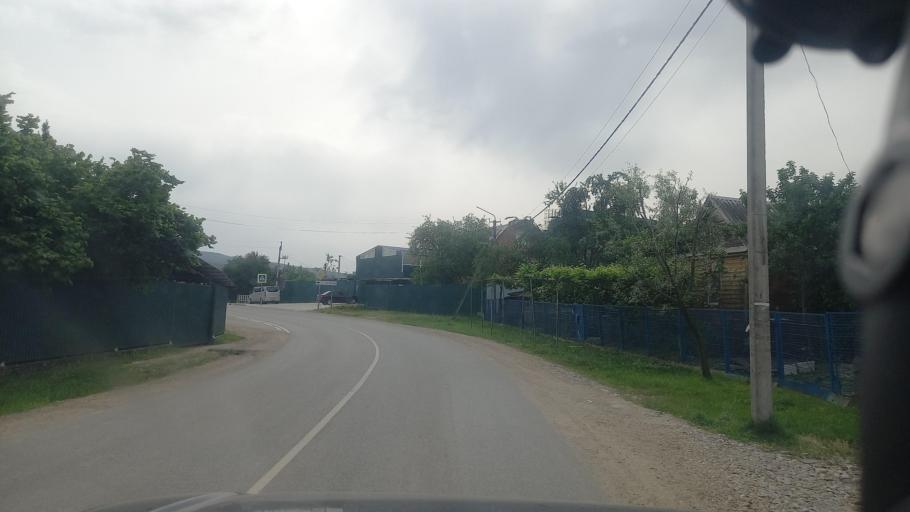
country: RU
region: Krasnodarskiy
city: Goryachiy Klyuch
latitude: 44.6063
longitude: 39.0224
